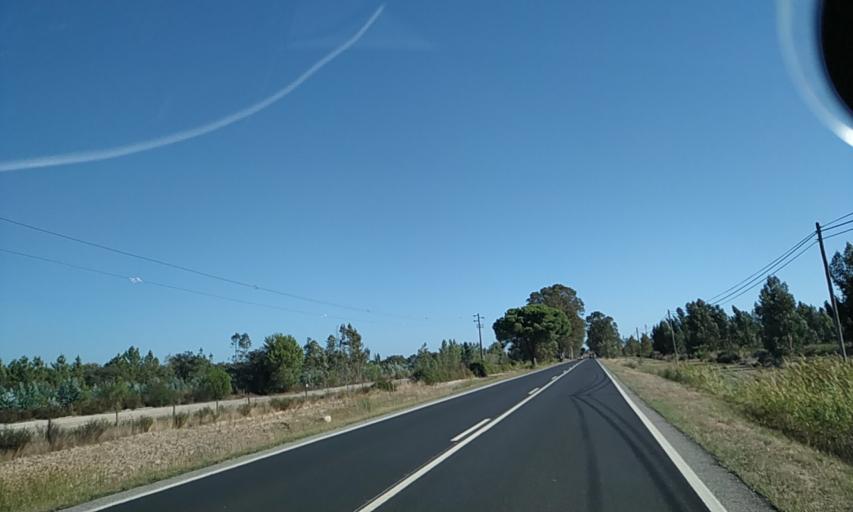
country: PT
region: Setubal
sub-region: Alcochete
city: Alcochete
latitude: 38.7926
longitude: -8.8808
